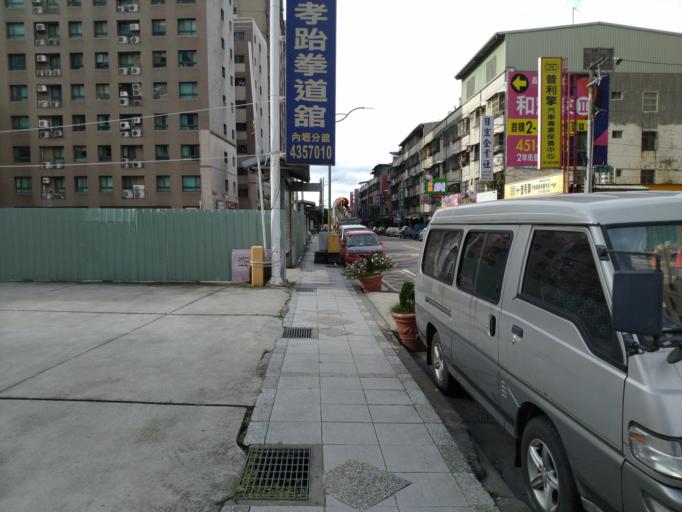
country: TW
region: Taiwan
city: Taoyuan City
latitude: 24.9777
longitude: 121.2516
